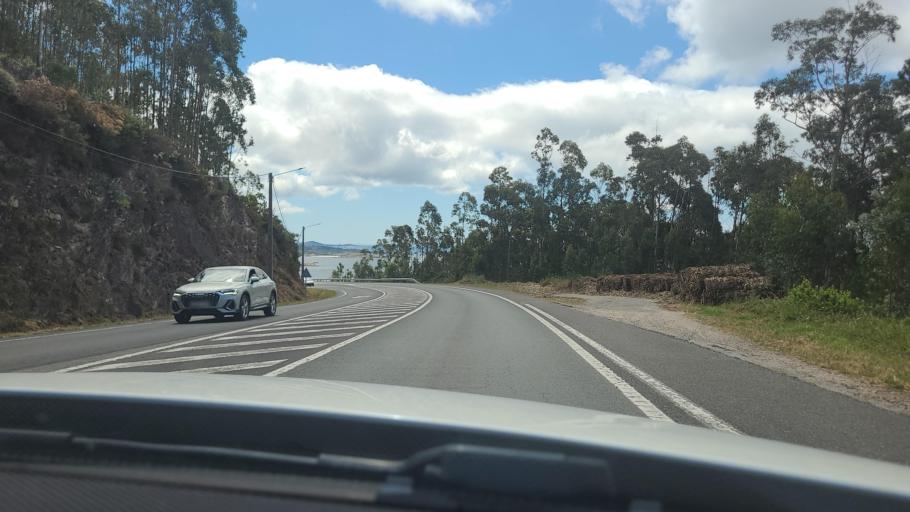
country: ES
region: Galicia
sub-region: Provincia da Coruna
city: Corcubion
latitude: 42.9147
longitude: -9.1456
